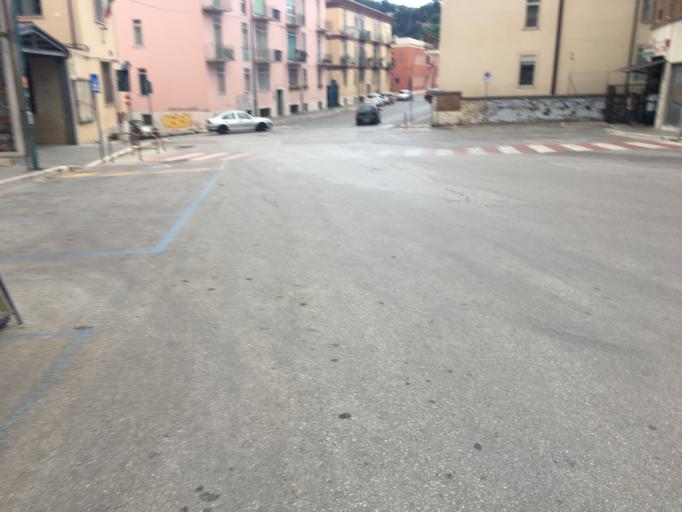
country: IT
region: Molise
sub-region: Provincia di Campobasso
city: Campobasso
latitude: 41.5565
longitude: 14.6567
